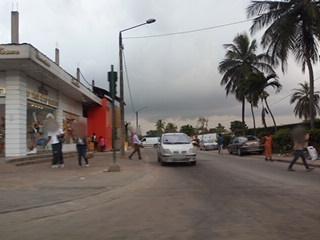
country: CI
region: Lagunes
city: Abobo
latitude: 5.3747
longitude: -3.9985
